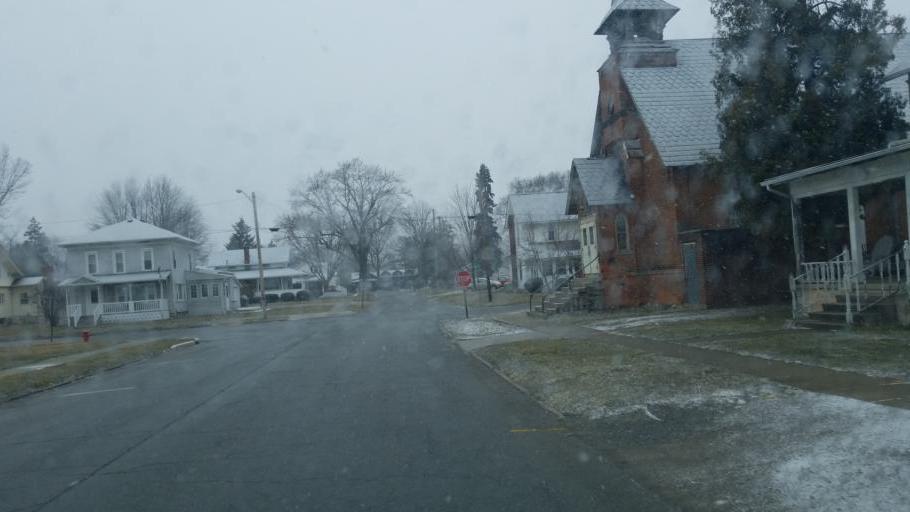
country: US
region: Ohio
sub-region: Defiance County
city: Hicksville
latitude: 41.2955
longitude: -84.7613
